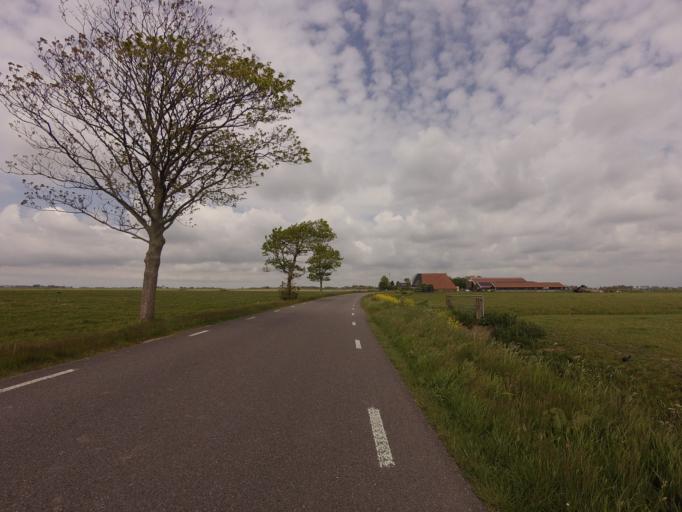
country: NL
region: Friesland
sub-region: Sudwest Fryslan
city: Bolsward
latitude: 53.0967
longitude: 5.5346
